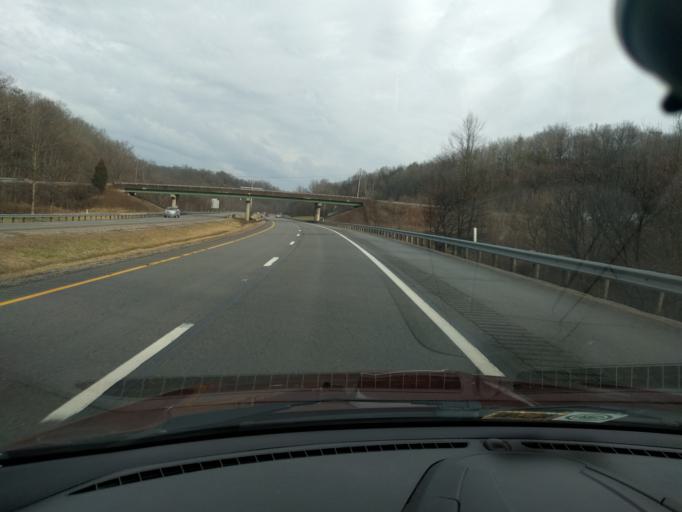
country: US
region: West Virginia
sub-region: Jackson County
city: Ravenswood
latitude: 38.9458
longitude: -81.7029
